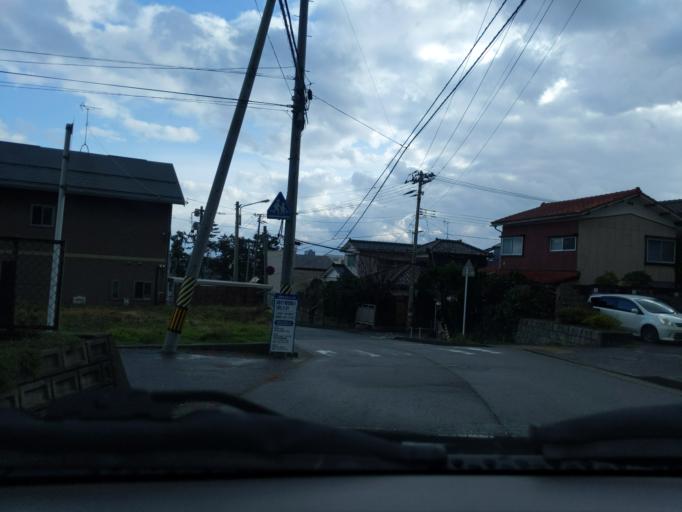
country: JP
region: Niigata
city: Niigata-shi
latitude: 37.9325
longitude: 139.0431
